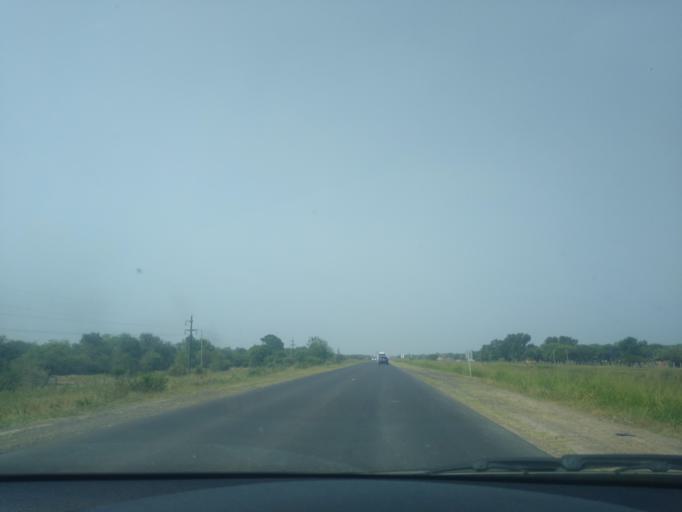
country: AR
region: Chaco
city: Fontana
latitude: -27.4928
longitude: -59.0758
